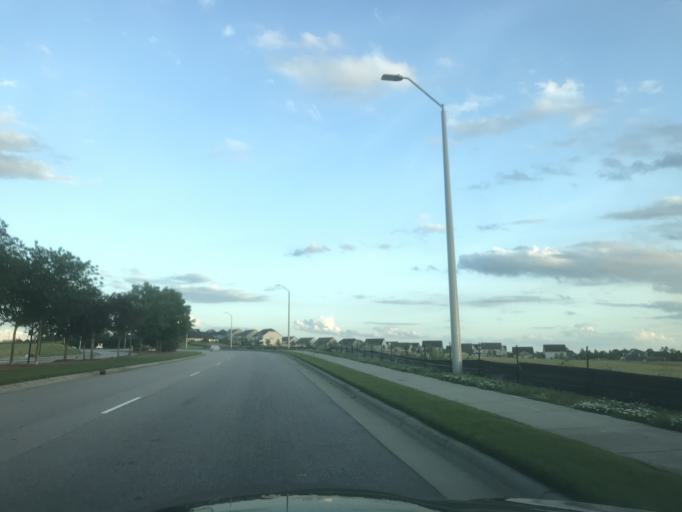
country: US
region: North Carolina
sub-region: Wake County
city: Knightdale
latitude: 35.7757
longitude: -78.4332
